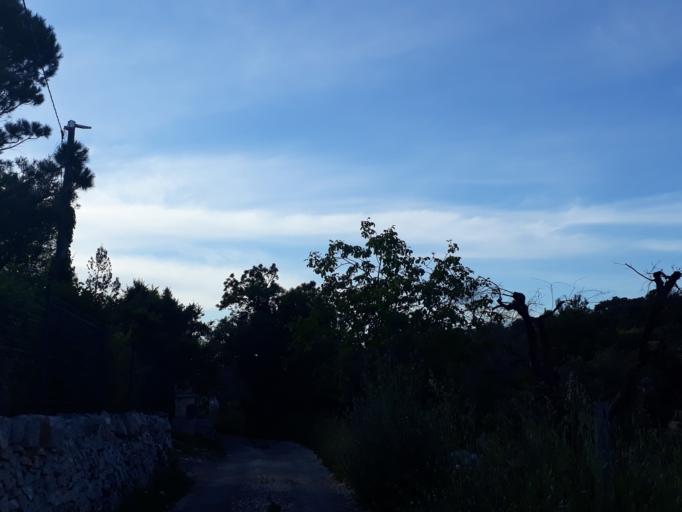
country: IT
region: Apulia
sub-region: Provincia di Brindisi
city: Lamie di Olimpie-Selva
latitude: 40.7990
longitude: 17.3452
